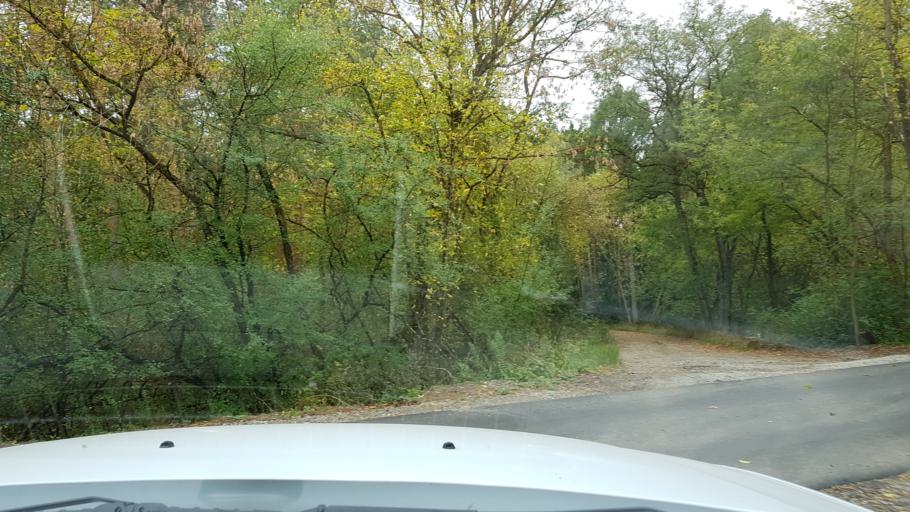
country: PL
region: West Pomeranian Voivodeship
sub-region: Powiat gryfinski
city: Cedynia
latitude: 52.8372
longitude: 14.2807
